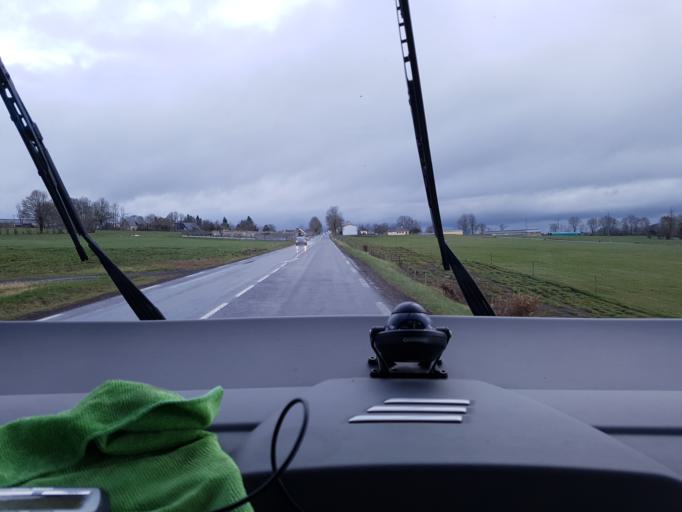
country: FR
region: Auvergne
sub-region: Departement du Puy-de-Dome
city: La Bourboule
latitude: 45.6540
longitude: 2.7405
